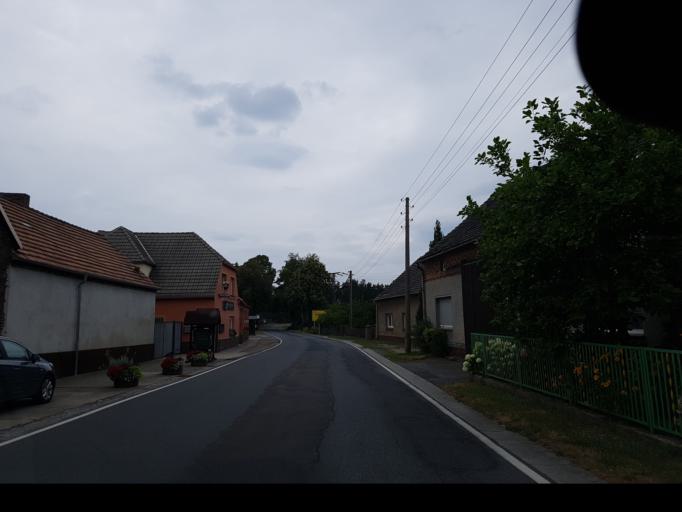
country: DE
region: Brandenburg
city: Sallgast
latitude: 51.6092
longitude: 13.8442
